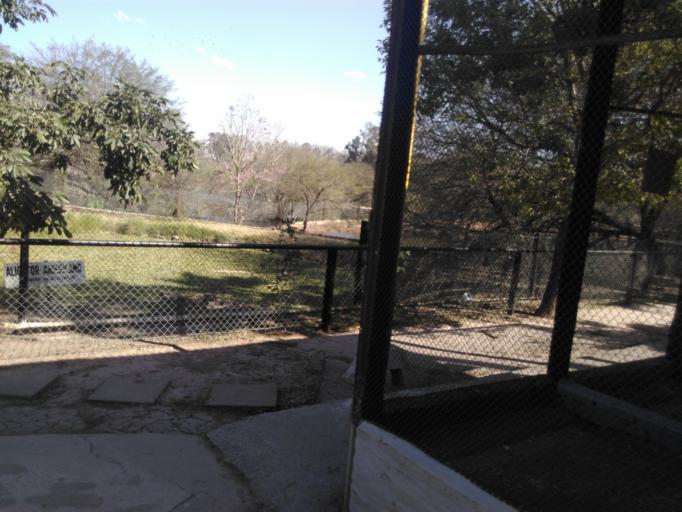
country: AR
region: Chaco
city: Presidencia Roque Saenz Pena
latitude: -26.8169
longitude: -60.4185
